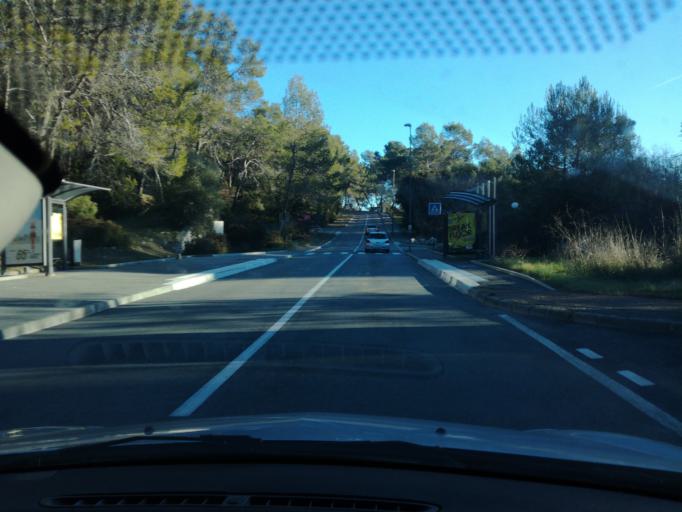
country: FR
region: Provence-Alpes-Cote d'Azur
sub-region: Departement des Alpes-Maritimes
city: Vallauris
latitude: 43.6110
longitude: 7.0514
